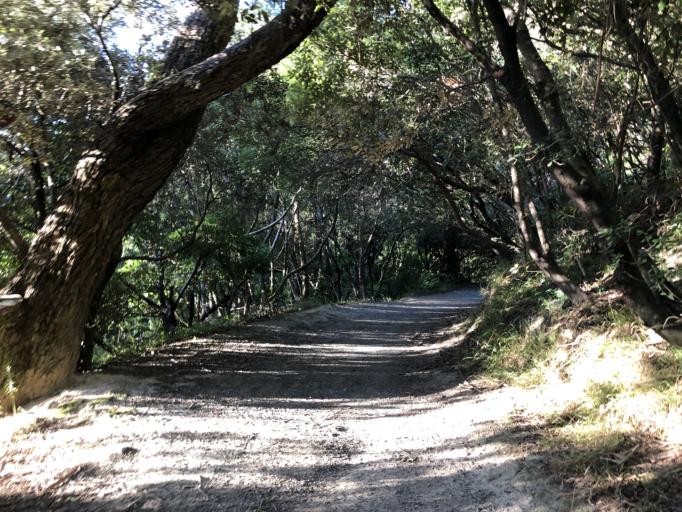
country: NZ
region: Wellington
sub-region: Wellington City
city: Wellington
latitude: -41.2979
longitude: 174.7904
